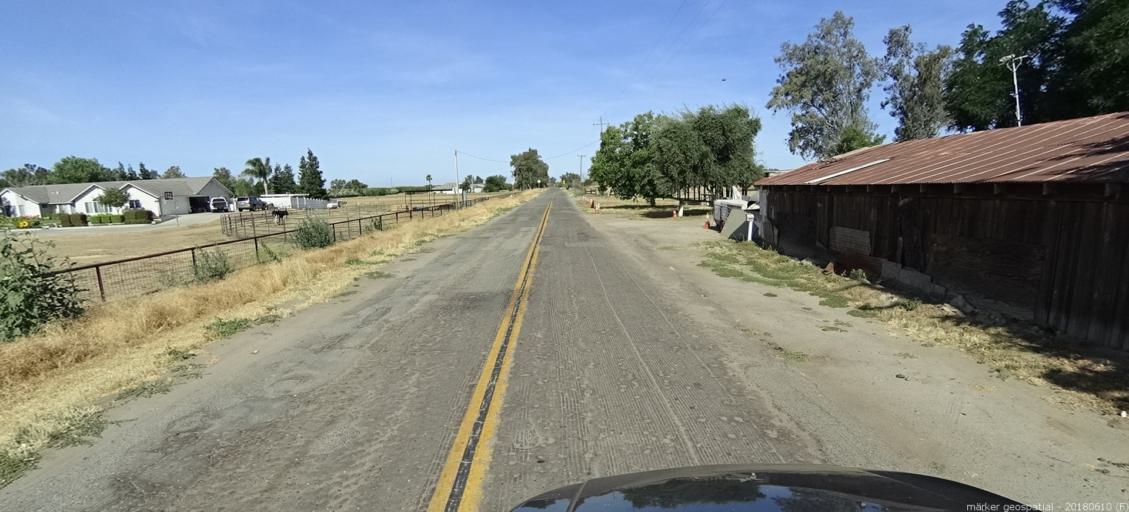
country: US
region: California
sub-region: Madera County
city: Chowchilla
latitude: 37.0983
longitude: -120.2569
